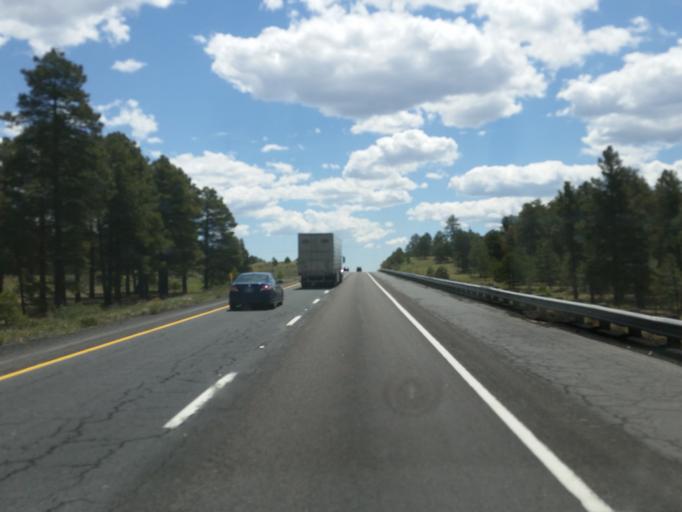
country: US
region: Arizona
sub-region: Coconino County
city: Parks
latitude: 35.2550
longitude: -112.0107
